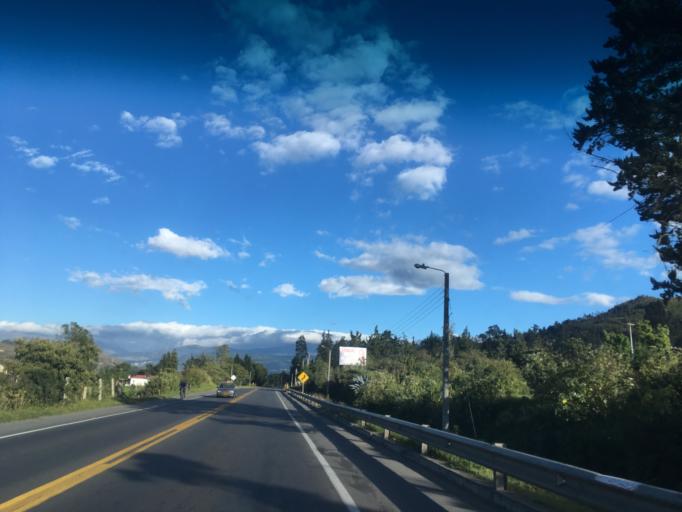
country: CO
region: Boyaca
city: Tibasosa
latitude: 5.7447
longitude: -72.9880
